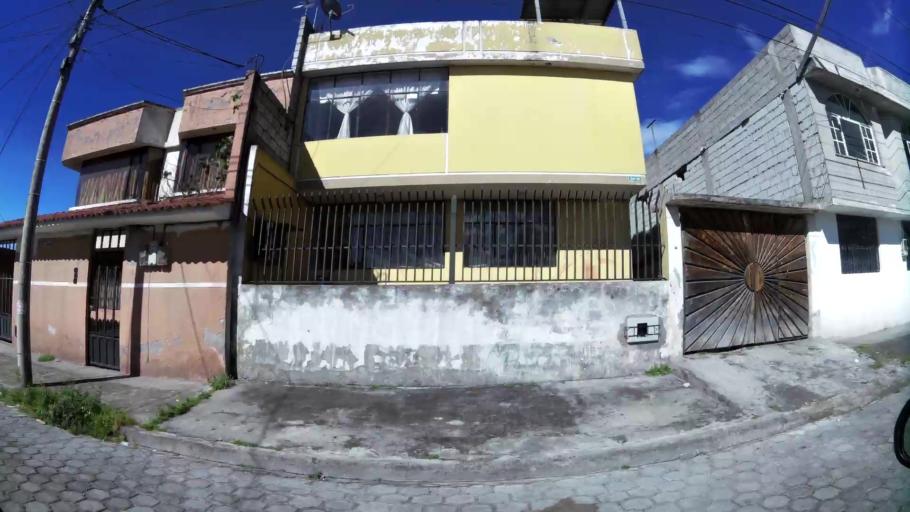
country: EC
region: Pichincha
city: Quito
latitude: -0.3020
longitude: -78.5611
